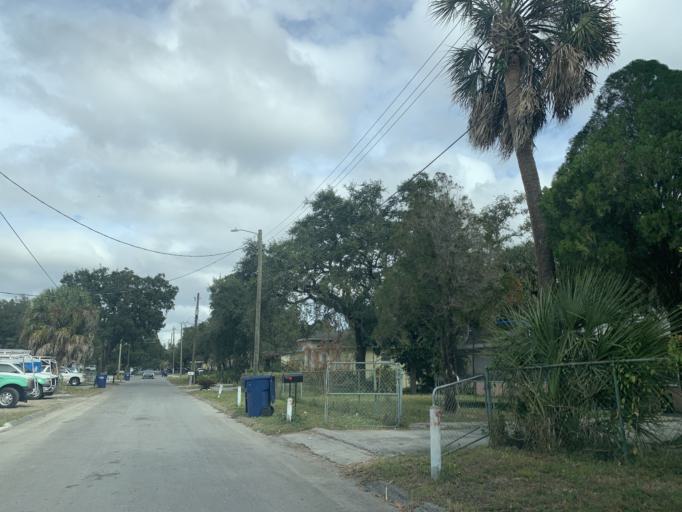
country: US
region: Florida
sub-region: Hillsborough County
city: East Lake-Orient Park
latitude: 27.9742
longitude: -82.3961
